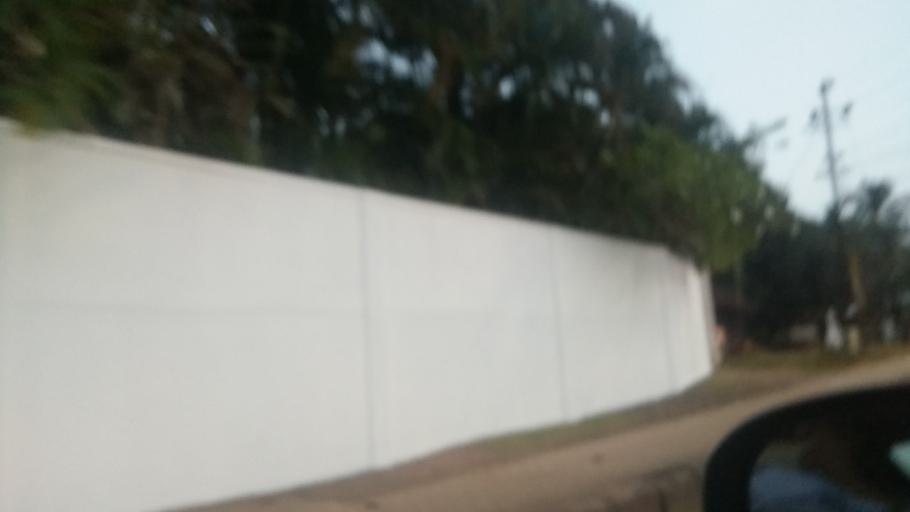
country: IN
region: Goa
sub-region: North Goa
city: Taleigao
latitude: 15.4685
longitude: 73.8199
